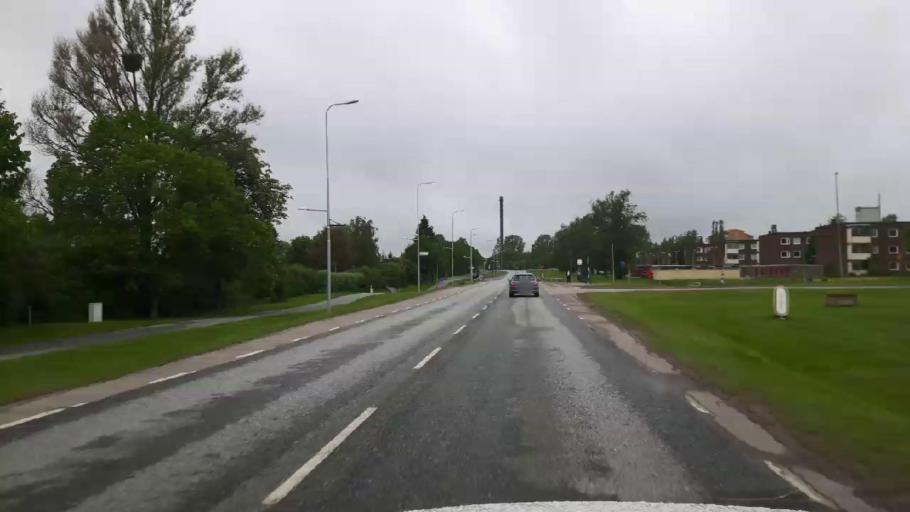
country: SE
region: Stockholm
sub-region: Upplands-Bro Kommun
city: Bro
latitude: 59.5116
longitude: 17.6504
